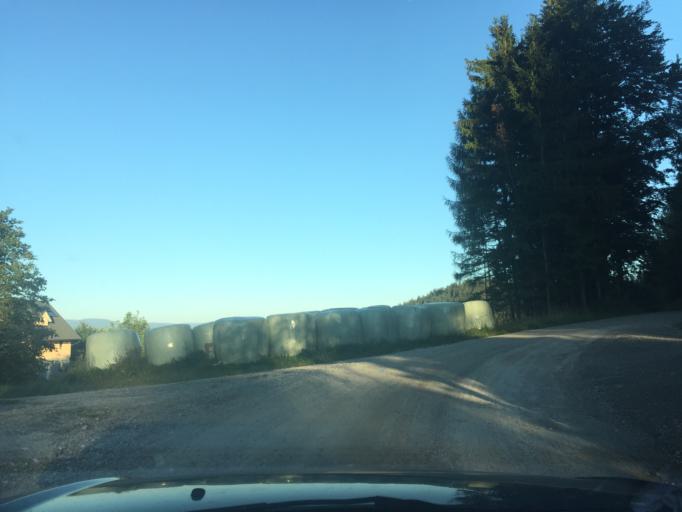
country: SI
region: Ravne na Koroskem
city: Kotlje
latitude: 46.4680
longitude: 14.9882
